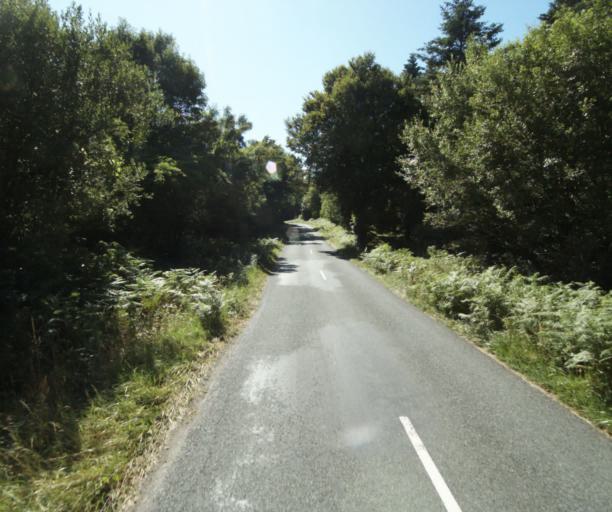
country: FR
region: Midi-Pyrenees
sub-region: Departement du Tarn
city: Dourgne
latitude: 43.4319
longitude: 2.1241
